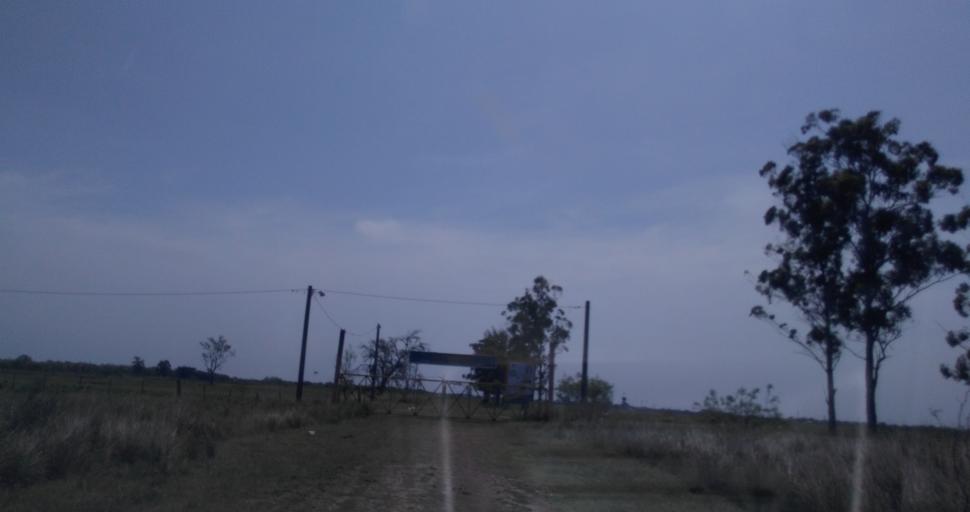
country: AR
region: Chaco
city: Fontana
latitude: -27.3946
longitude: -58.9989
